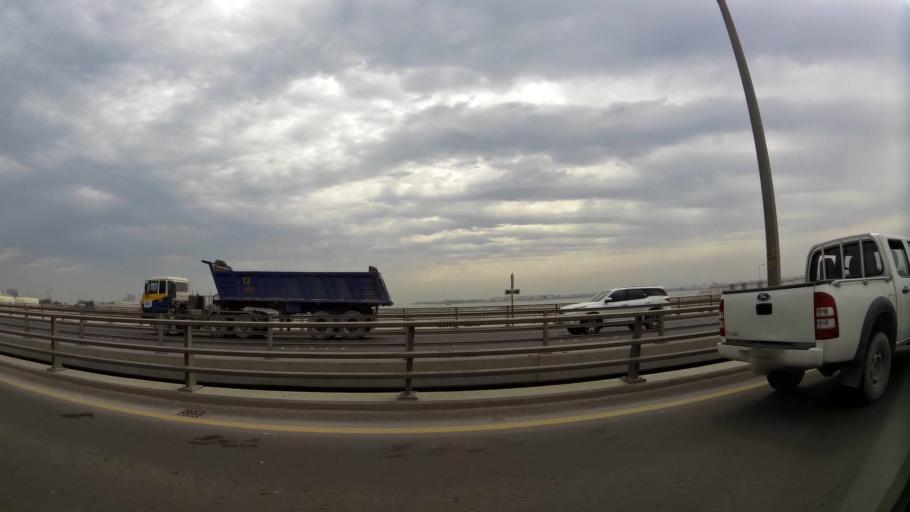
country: BH
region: Manama
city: Manama
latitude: 26.1934
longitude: 50.5888
